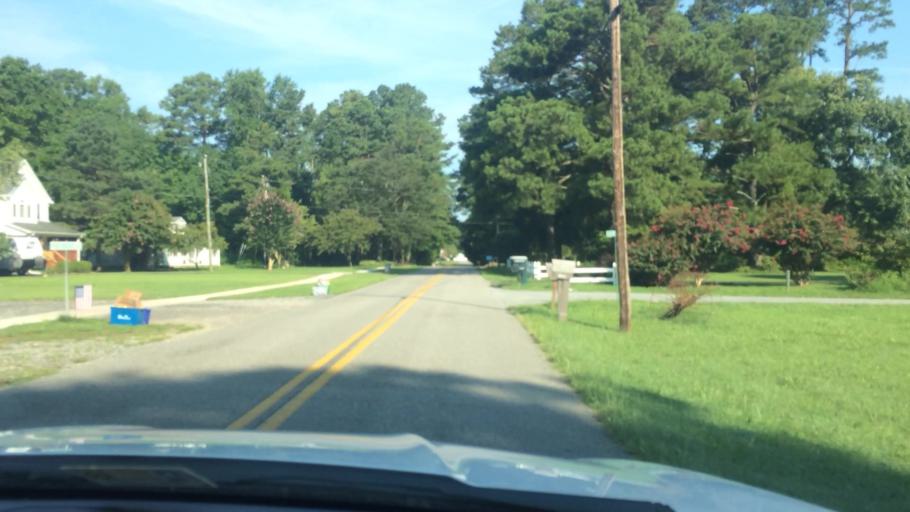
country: US
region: Virginia
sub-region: King William County
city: West Point
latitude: 37.5642
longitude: -76.7994
